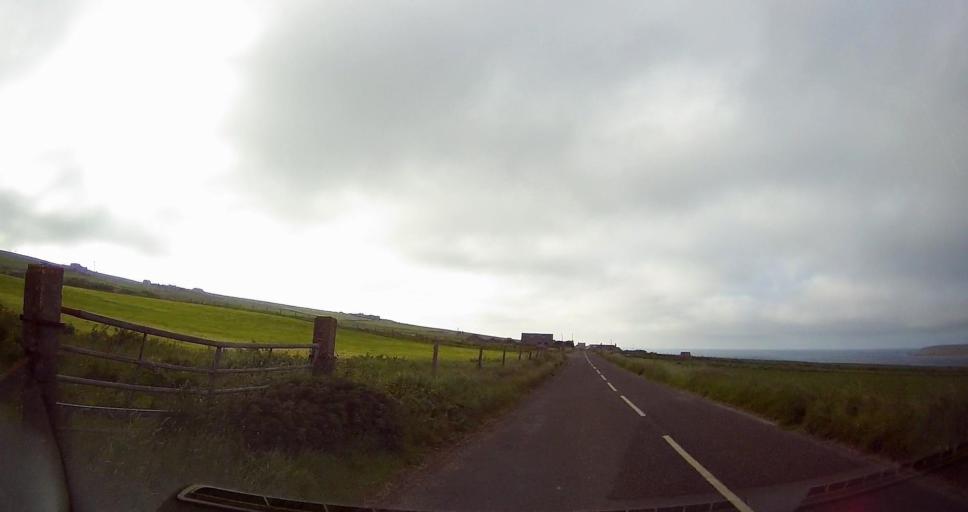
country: GB
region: Scotland
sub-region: Orkney Islands
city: Orkney
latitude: 59.1205
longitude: -3.1226
